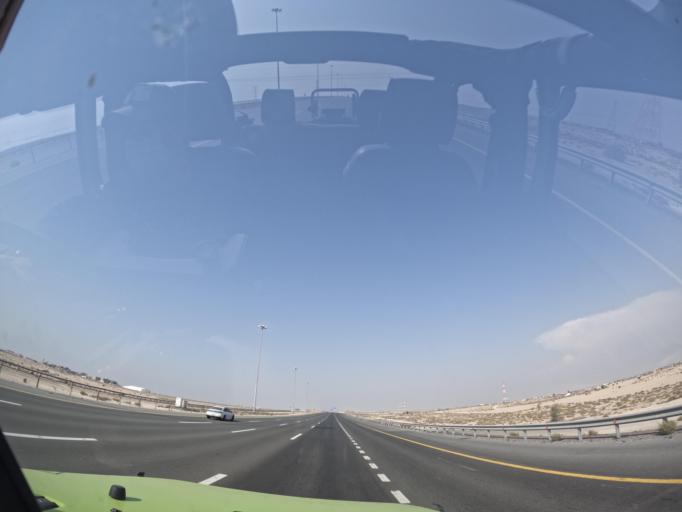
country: AE
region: Abu Dhabi
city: Abu Dhabi
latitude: 24.6531
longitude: 54.7964
